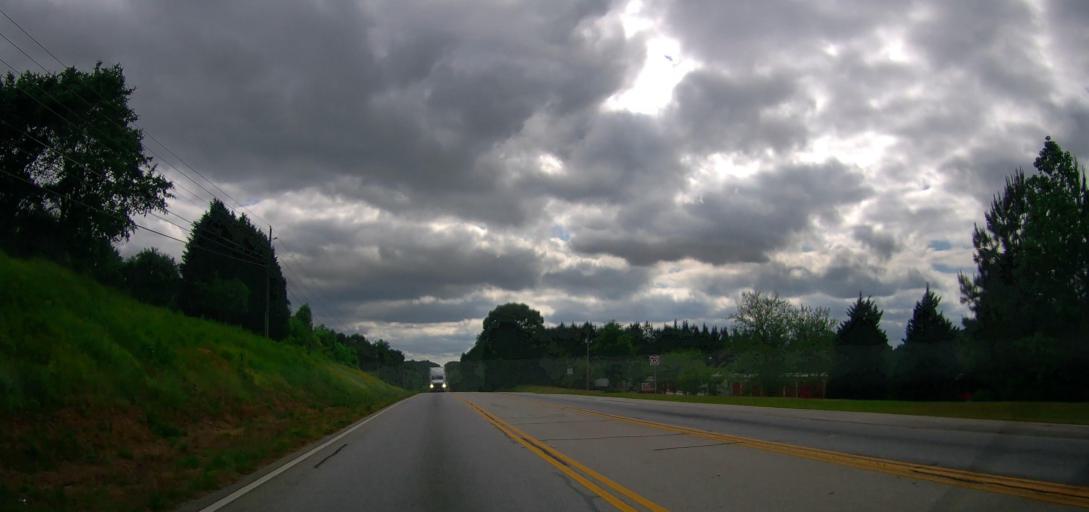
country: US
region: Georgia
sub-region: Walton County
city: Walnut Grove
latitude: 33.7703
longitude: -83.7974
